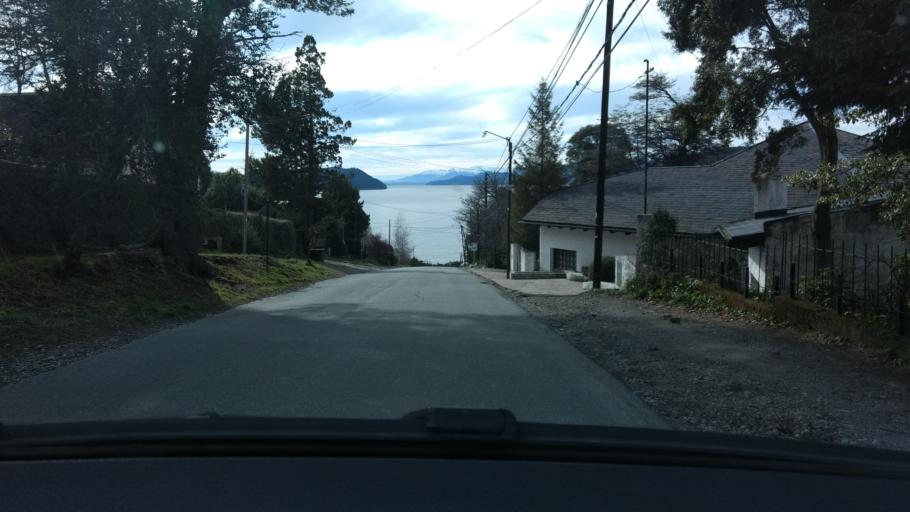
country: AR
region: Rio Negro
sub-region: Departamento de Bariloche
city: San Carlos de Bariloche
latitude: -41.1236
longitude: -71.3971
